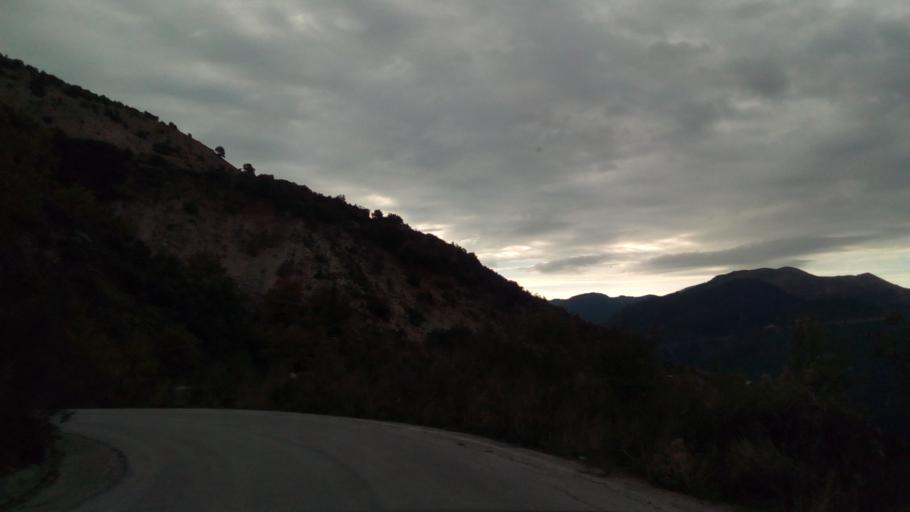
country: GR
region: West Greece
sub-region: Nomos Aitolias kai Akarnanias
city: Thermo
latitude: 38.6049
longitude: 21.8020
